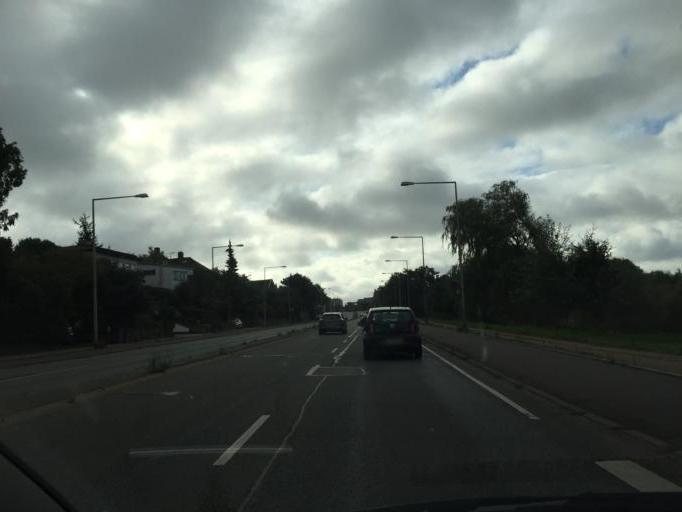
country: DK
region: Capital Region
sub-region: Kobenhavn
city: Vanlose
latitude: 55.7123
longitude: 12.5050
